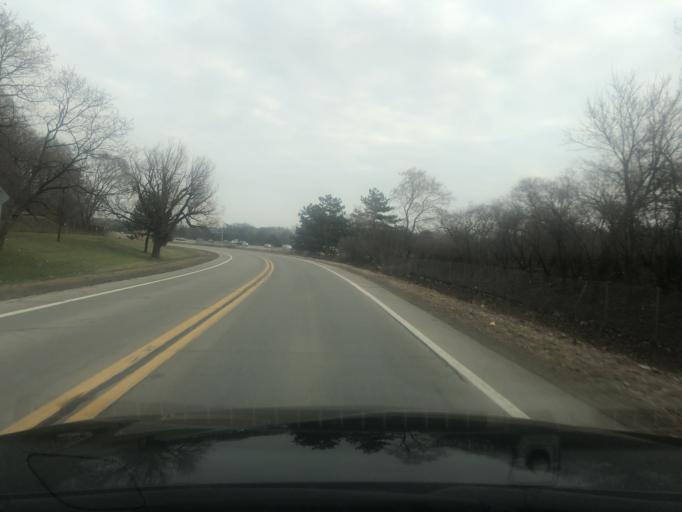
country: US
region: Michigan
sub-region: Wayne County
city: Belleville
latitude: 42.2201
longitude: -83.5165
